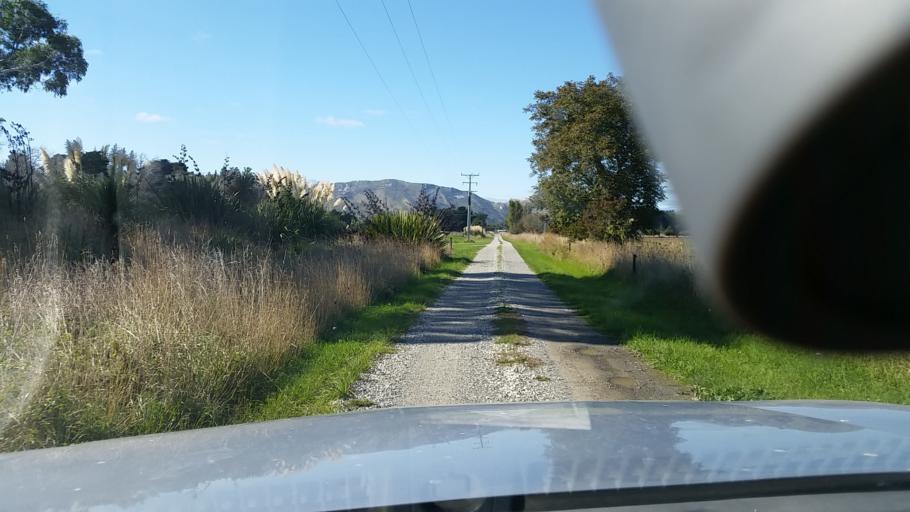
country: NZ
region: Marlborough
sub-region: Marlborough District
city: Blenheim
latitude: -41.8245
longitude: 174.1197
